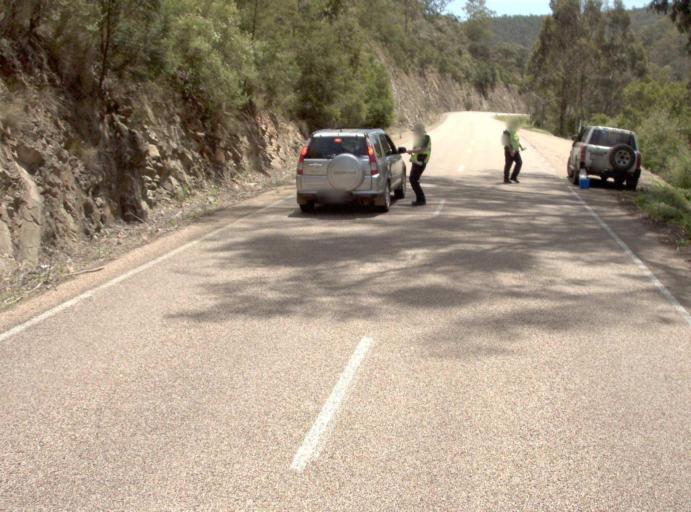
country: AU
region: Victoria
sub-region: East Gippsland
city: Lakes Entrance
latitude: -37.5444
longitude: 147.8659
